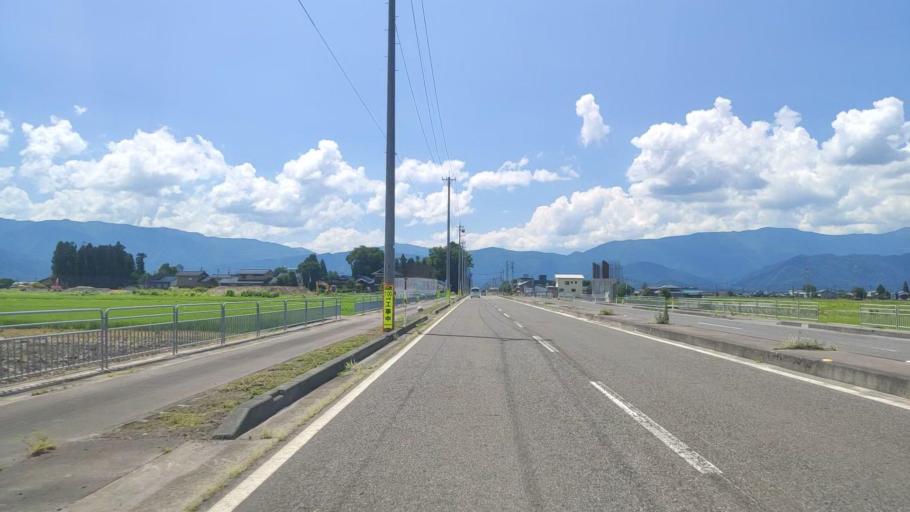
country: JP
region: Fukui
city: Ono
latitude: 35.9991
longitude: 136.5091
